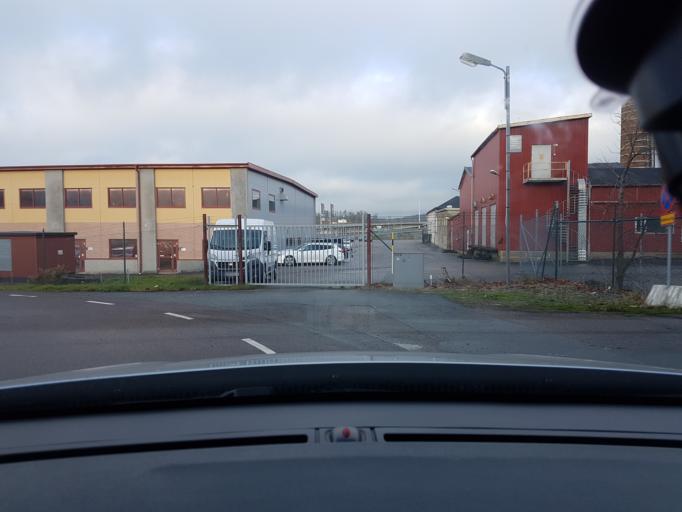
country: SE
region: Vaestra Goetaland
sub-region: Ale Kommun
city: Alafors
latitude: 57.9189
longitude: 12.0681
